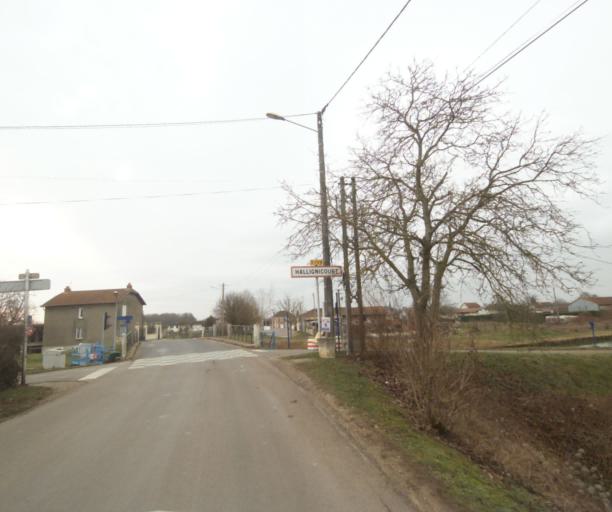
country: FR
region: Champagne-Ardenne
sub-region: Departement de la Haute-Marne
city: Villiers-en-Lieu
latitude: 48.6457
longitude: 4.8729
